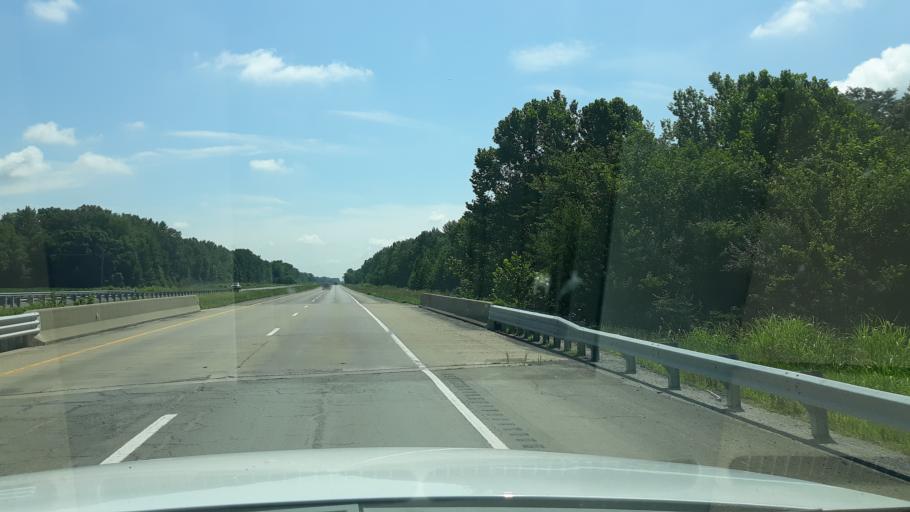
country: US
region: Illinois
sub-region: Saline County
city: Carrier Mills
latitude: 37.7333
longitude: -88.6693
